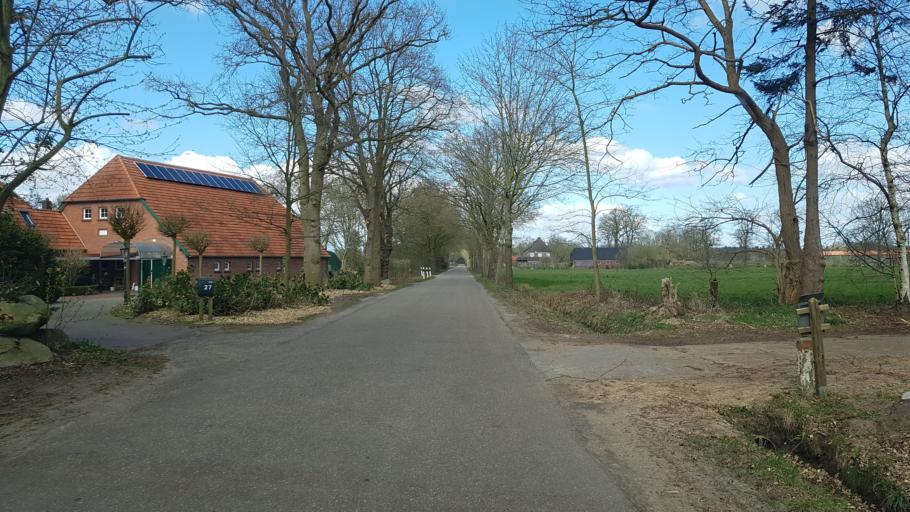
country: DE
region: Lower Saxony
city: Edewecht
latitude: 53.1633
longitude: 7.9372
